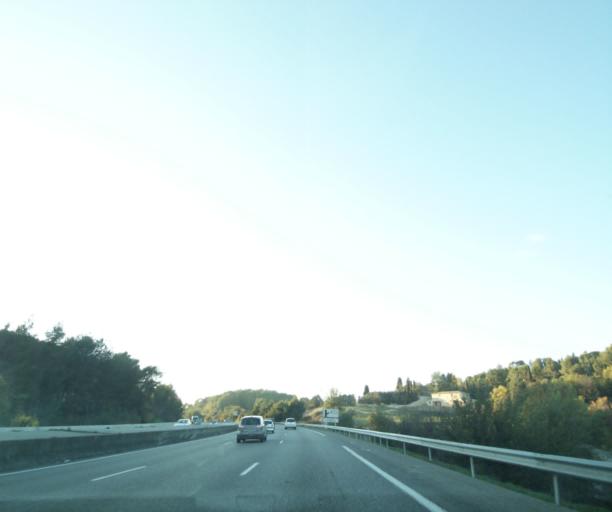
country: FR
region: Provence-Alpes-Cote d'Azur
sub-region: Departement des Bouches-du-Rhone
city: Le Tholonet
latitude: 43.5124
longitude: 5.4942
